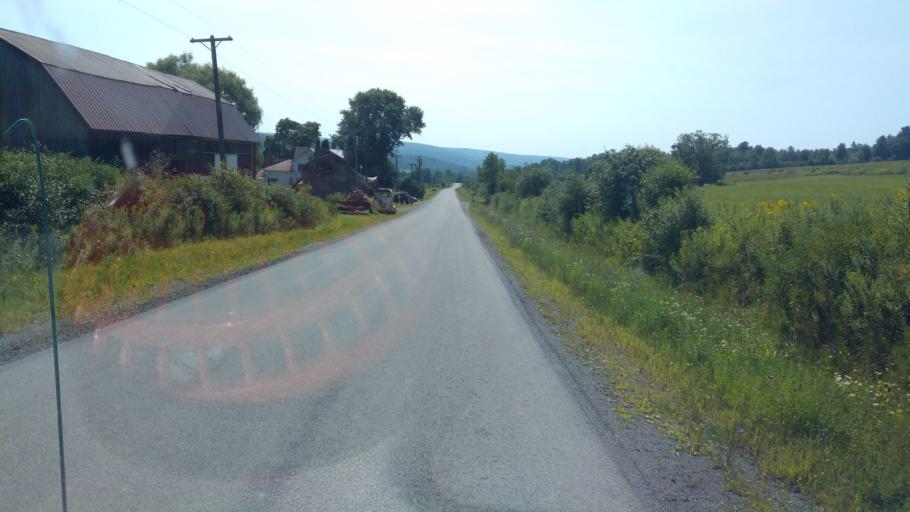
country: US
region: New York
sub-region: Allegany County
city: Belmont
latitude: 42.3398
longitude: -78.0411
